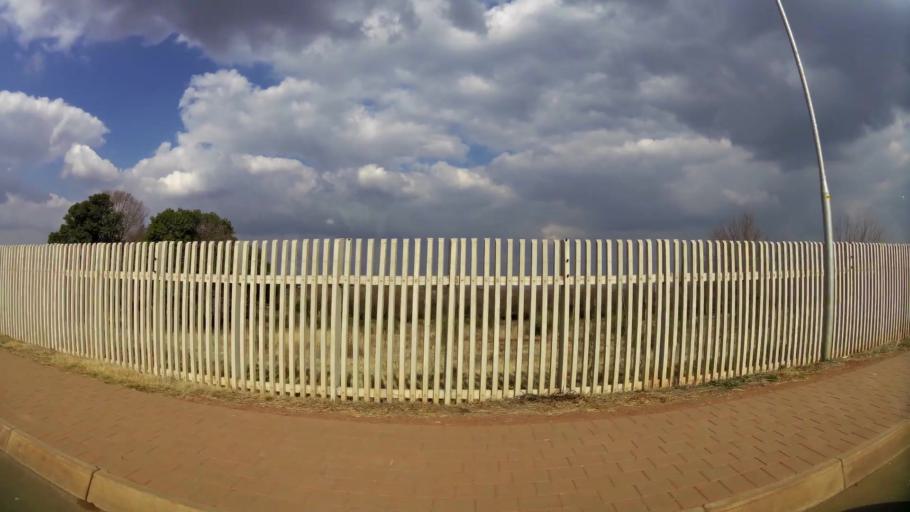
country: ZA
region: Gauteng
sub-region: Ekurhuleni Metropolitan Municipality
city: Tembisa
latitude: -25.9347
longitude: 28.2069
